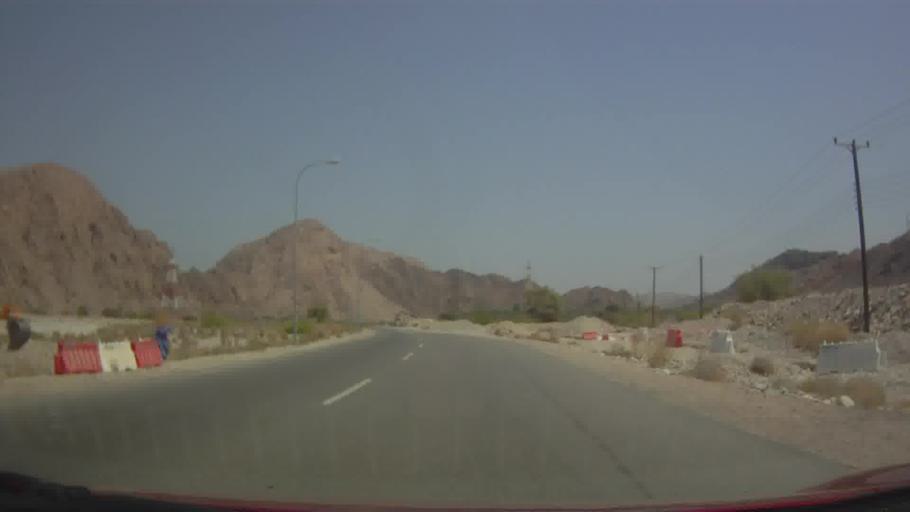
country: OM
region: Muhafazat Masqat
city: Muscat
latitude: 23.5095
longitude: 58.6390
